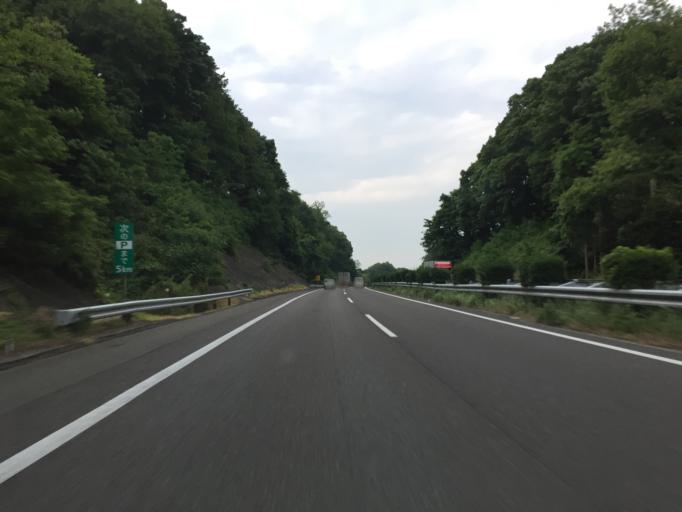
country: JP
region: Fukushima
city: Sukagawa
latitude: 37.2167
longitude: 140.3097
